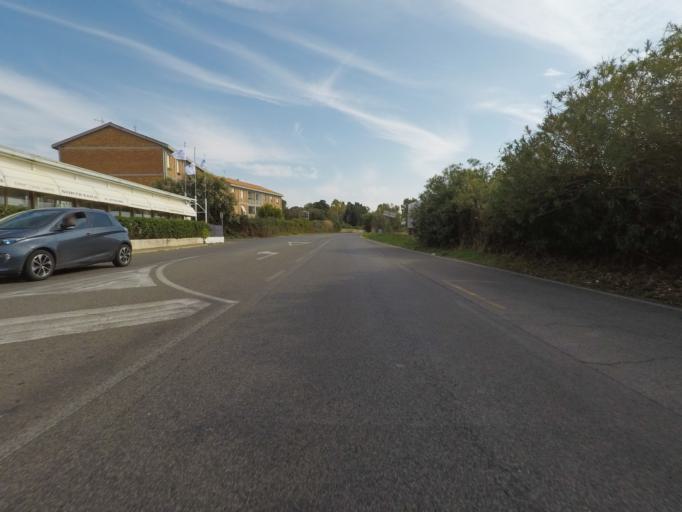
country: IT
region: Latium
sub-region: Citta metropolitana di Roma Capitale
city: Civitavecchia
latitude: 42.0612
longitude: 11.8163
